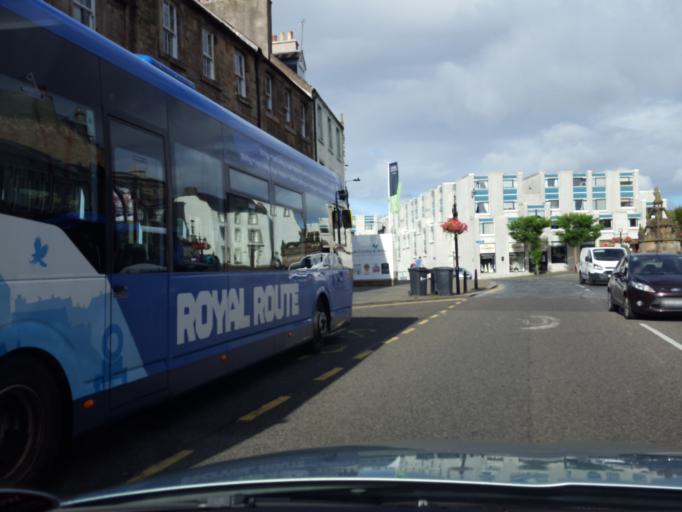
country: GB
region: Scotland
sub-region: West Lothian
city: Linlithgow
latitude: 55.9769
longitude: -3.5995
